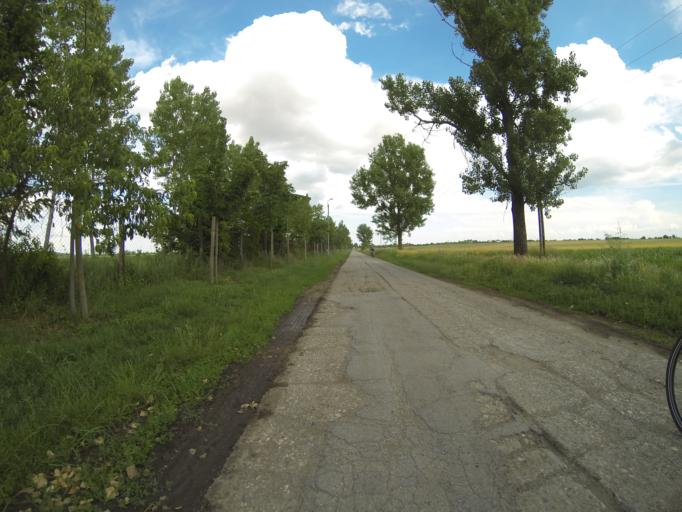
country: RO
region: Dolj
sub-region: Comuna Segarcea
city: Segarcea
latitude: 44.1090
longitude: 23.7300
